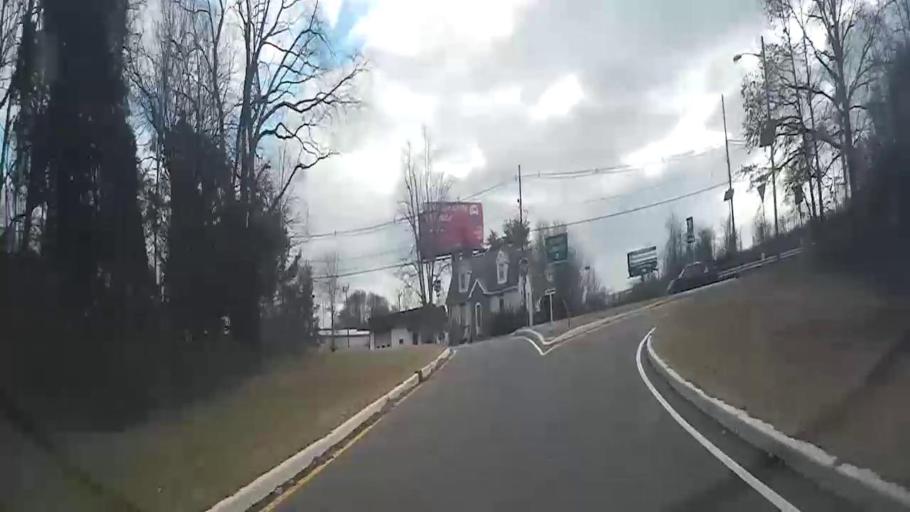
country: US
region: New Jersey
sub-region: Camden County
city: Blackwood
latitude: 39.8116
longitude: -75.0609
